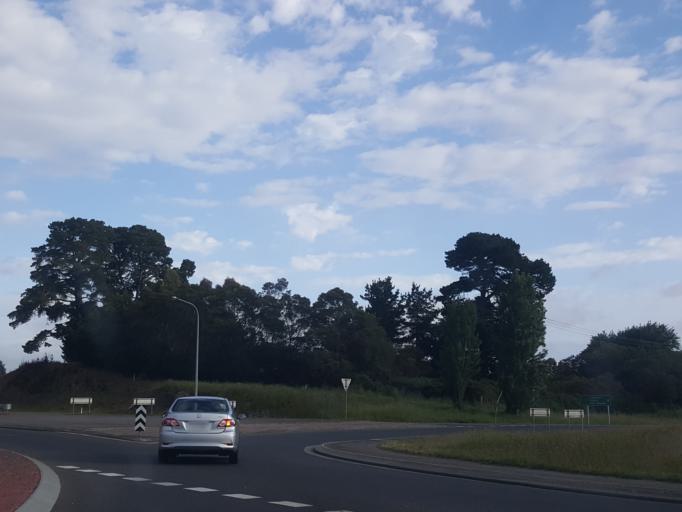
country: AU
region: Tasmania
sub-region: Northern Midlands
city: Perth
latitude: -41.5314
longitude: 147.1866
